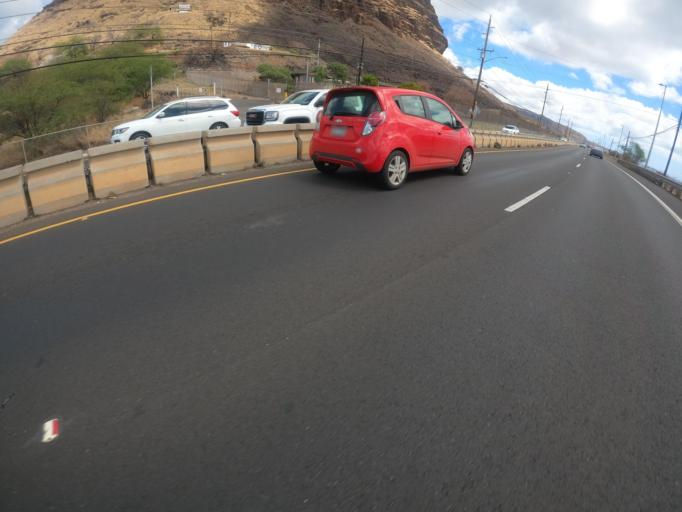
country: US
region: Hawaii
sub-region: Honolulu County
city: Ma'ili
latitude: 21.4013
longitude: -158.1753
